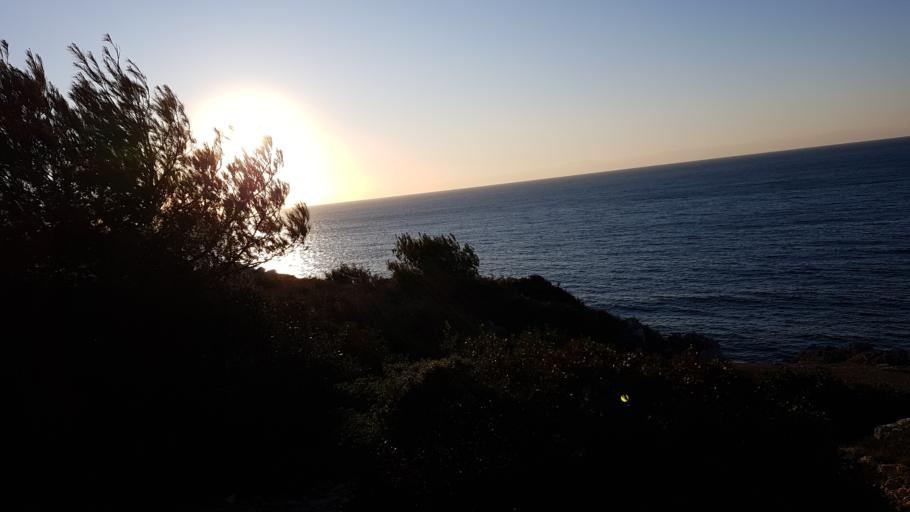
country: IT
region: Apulia
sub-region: Provincia di Lecce
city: Nardo
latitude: 40.1548
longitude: 17.9606
